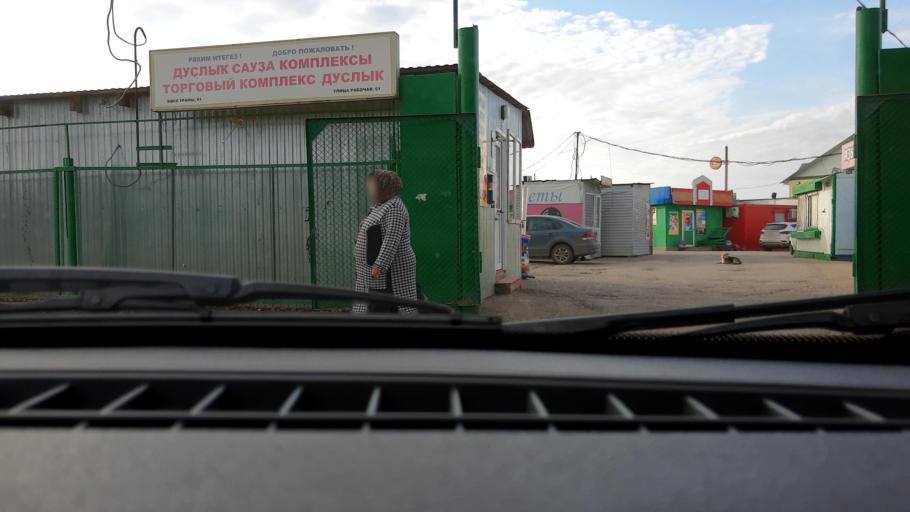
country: RU
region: Bashkortostan
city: Ufa
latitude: 54.7451
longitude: 55.9152
